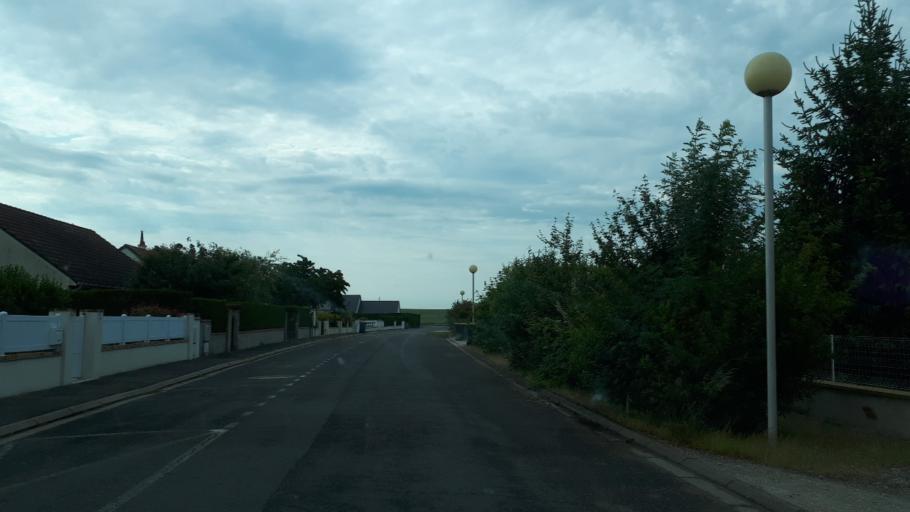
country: FR
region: Centre
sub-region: Departement du Loir-et-Cher
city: Naveil
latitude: 47.7700
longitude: 1.0111
